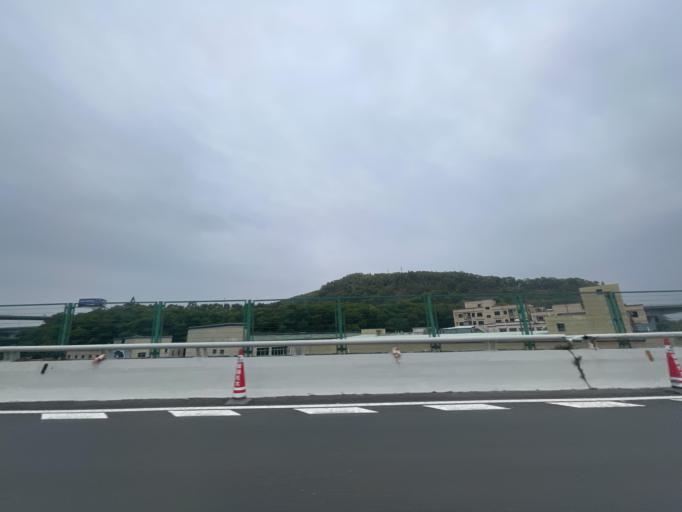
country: CN
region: Guangdong
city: Humen
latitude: 22.8072
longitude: 113.6447
